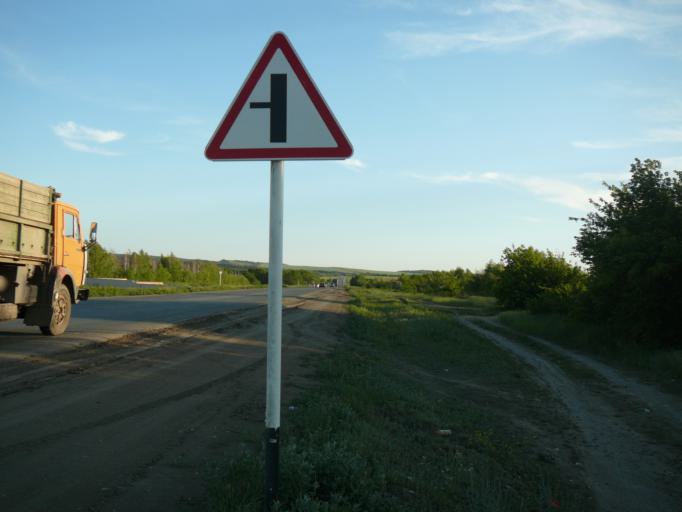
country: RU
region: Saratov
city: Sokolovyy
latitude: 51.6336
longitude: 45.7966
